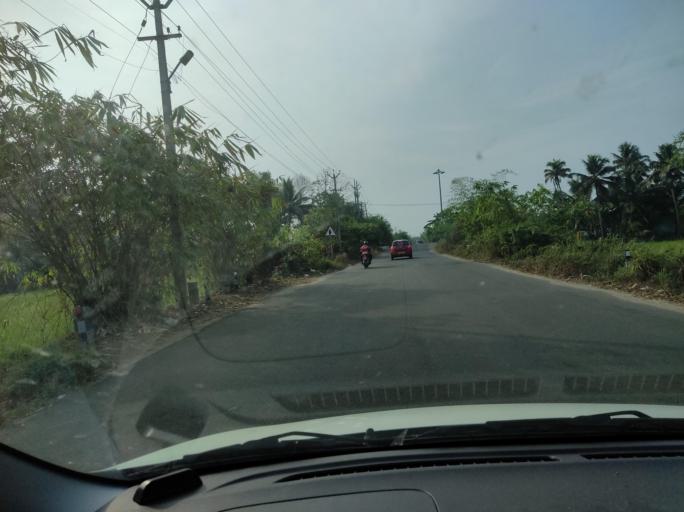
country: IN
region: Kerala
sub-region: Kottayam
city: Kottayam
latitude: 9.5660
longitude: 76.5064
